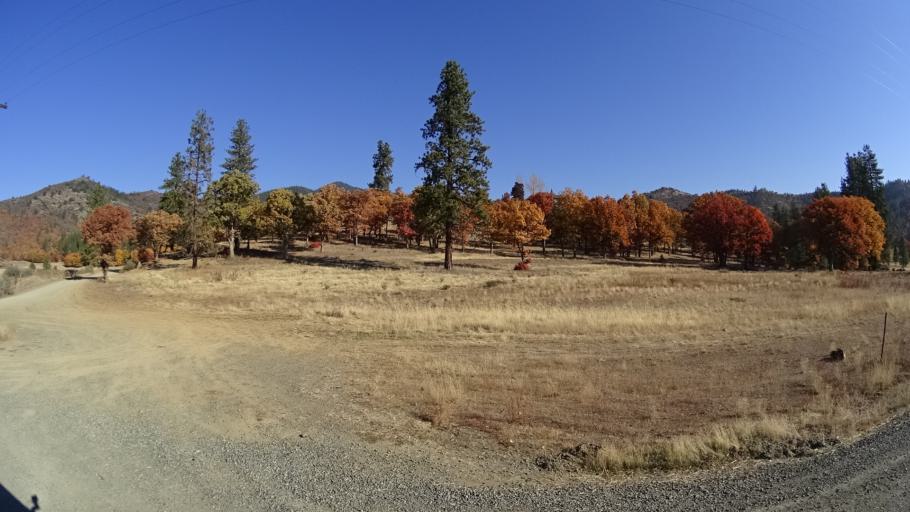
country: US
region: California
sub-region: Siskiyou County
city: Yreka
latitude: 41.6412
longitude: -122.9196
